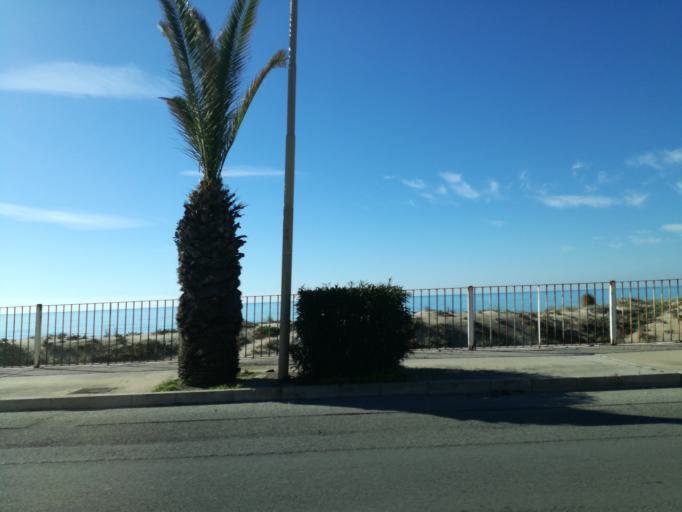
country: IT
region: Sicily
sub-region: Provincia di Caltanissetta
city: Gela
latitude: 37.0700
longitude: 14.2224
